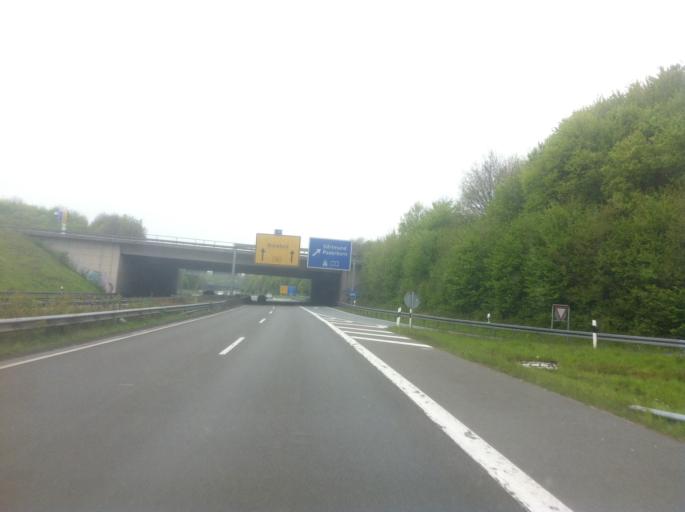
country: DE
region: North Rhine-Westphalia
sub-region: Regierungsbezirk Detmold
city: Oerlinghausen
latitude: 51.9950
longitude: 8.6203
